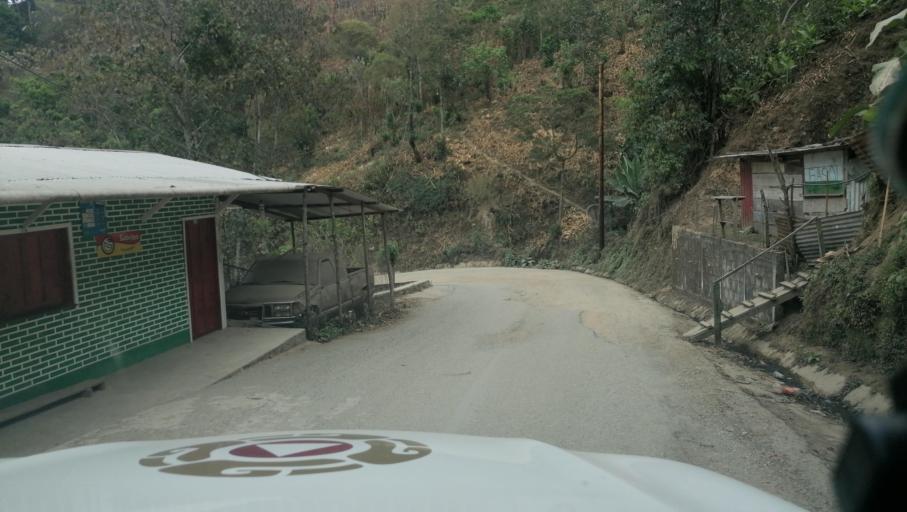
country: GT
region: San Marcos
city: Tacana
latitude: 15.2058
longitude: -92.1906
